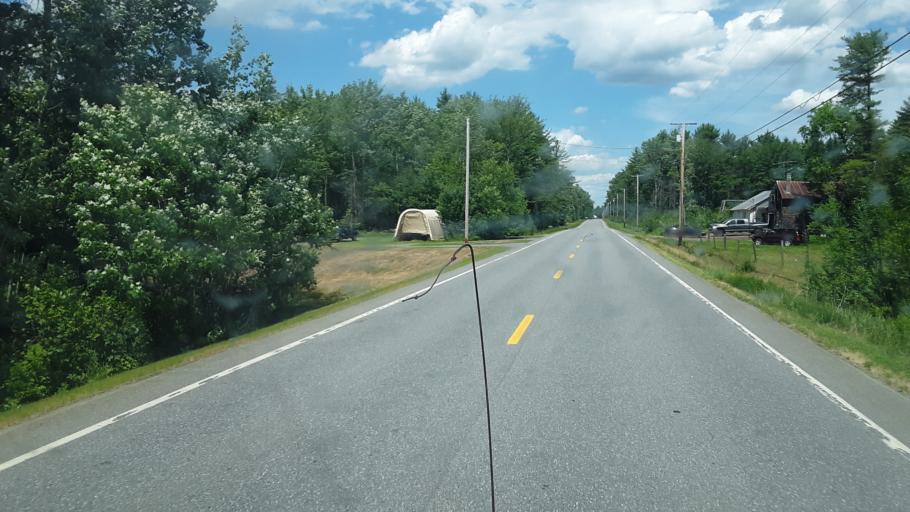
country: US
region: Maine
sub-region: Franklin County
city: Chesterville
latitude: 44.6001
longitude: -70.1092
